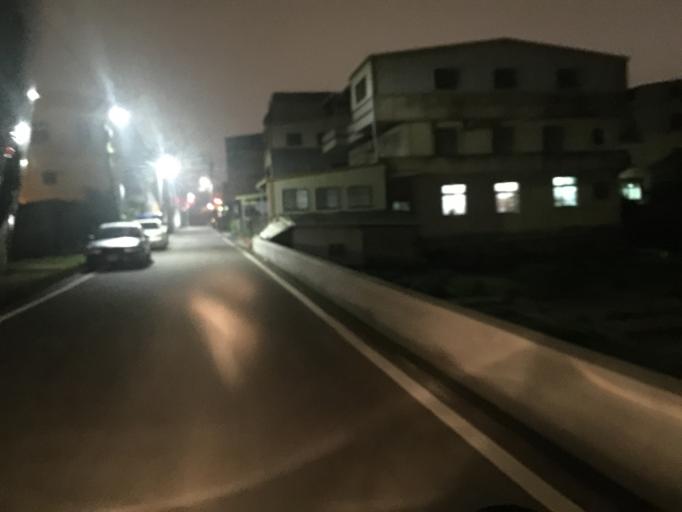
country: TW
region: Taiwan
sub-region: Miaoli
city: Miaoli
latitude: 24.5787
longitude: 120.8285
